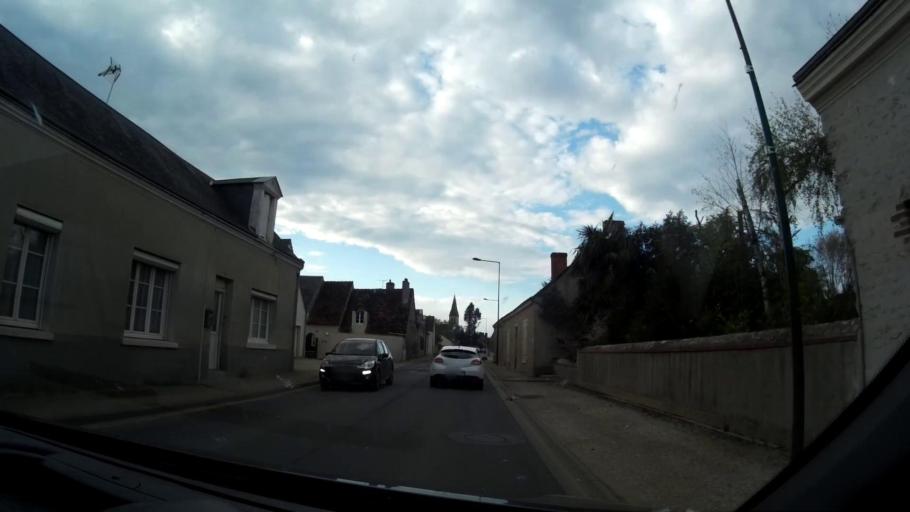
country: FR
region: Centre
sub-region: Departement du Loir-et-Cher
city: Cormeray
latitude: 47.4875
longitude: 1.4088
